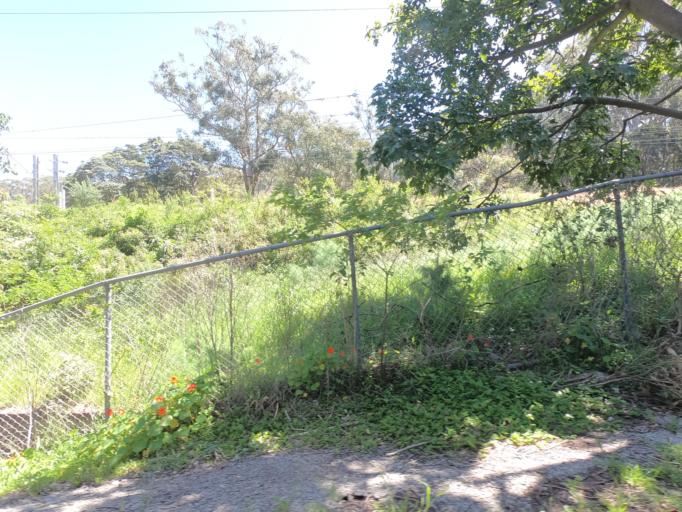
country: AU
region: New South Wales
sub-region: Wollongong
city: Bulli
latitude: -34.3050
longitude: 150.9315
